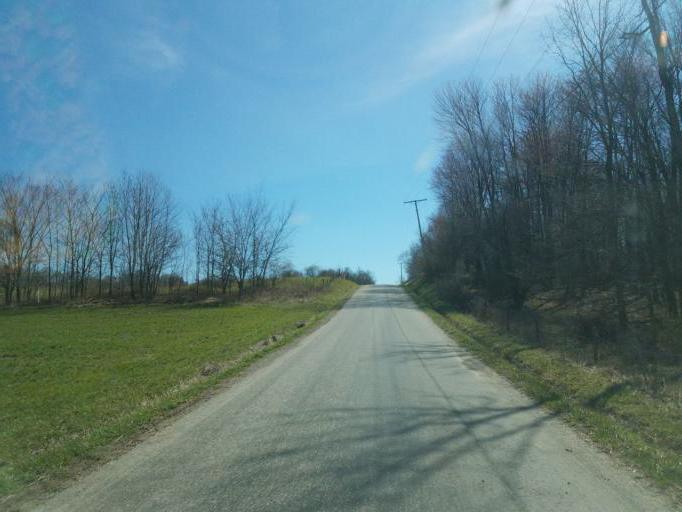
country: US
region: Ohio
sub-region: Ashland County
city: Ashland
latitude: 40.8977
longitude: -82.3585
